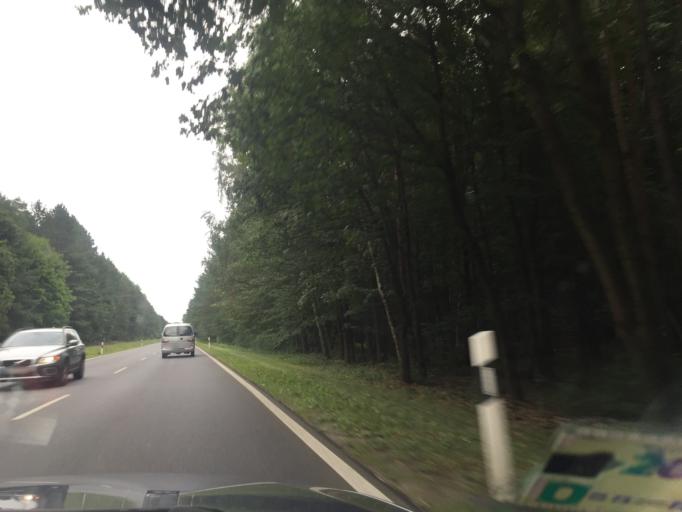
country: DE
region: Brandenburg
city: Wandlitz
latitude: 52.7276
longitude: 13.5131
